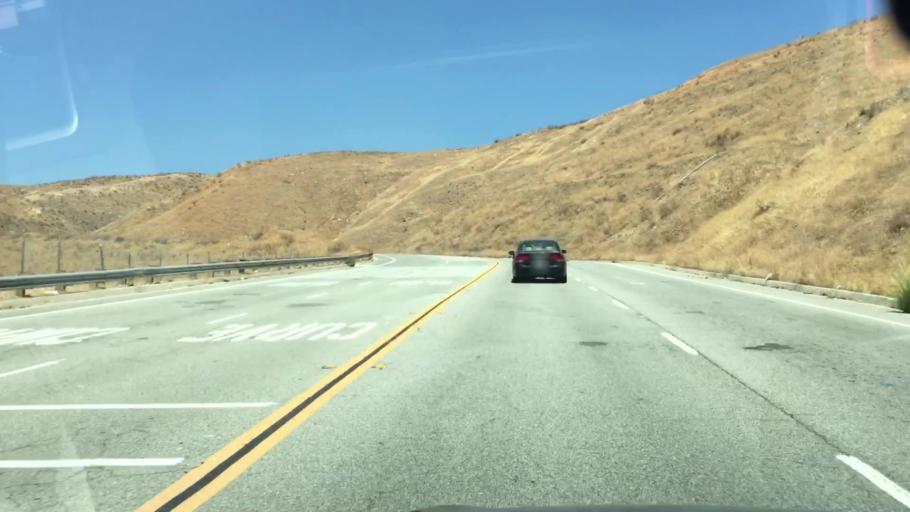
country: US
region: California
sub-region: San Bernardino County
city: Muscoy
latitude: 34.1564
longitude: -117.3217
